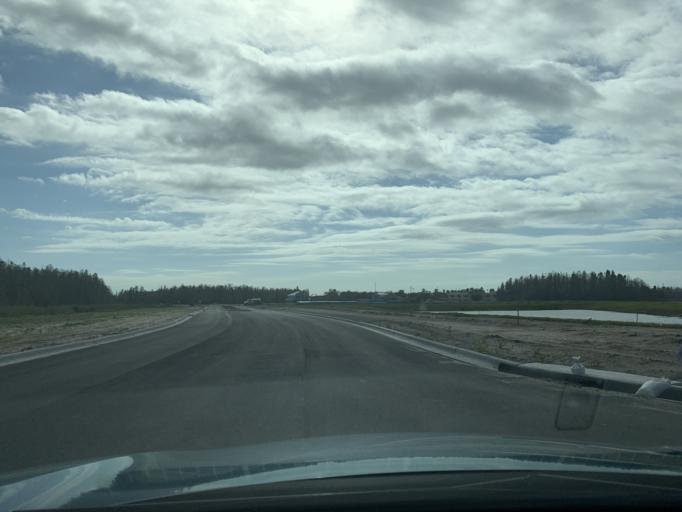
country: US
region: Florida
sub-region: Pasco County
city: Trinity
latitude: 28.2015
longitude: -82.6712
